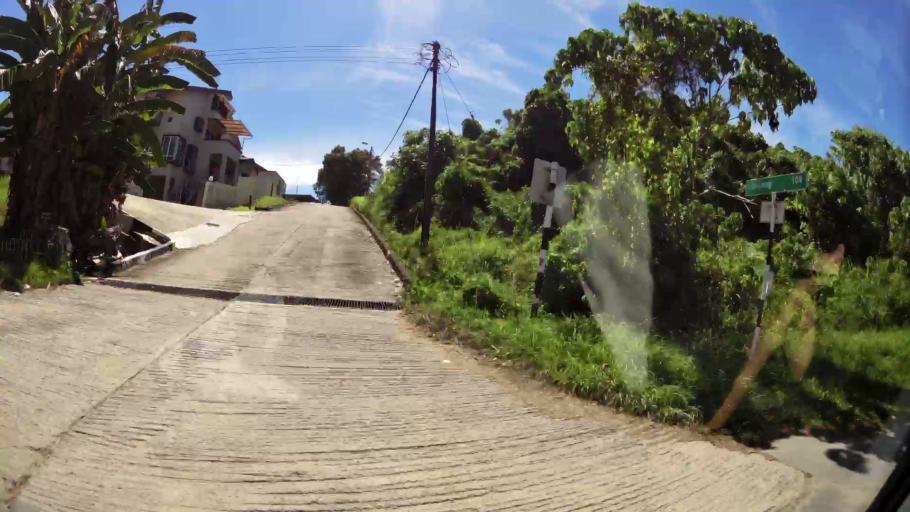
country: BN
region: Brunei and Muara
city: Bandar Seri Begawan
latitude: 5.0211
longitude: 115.0581
